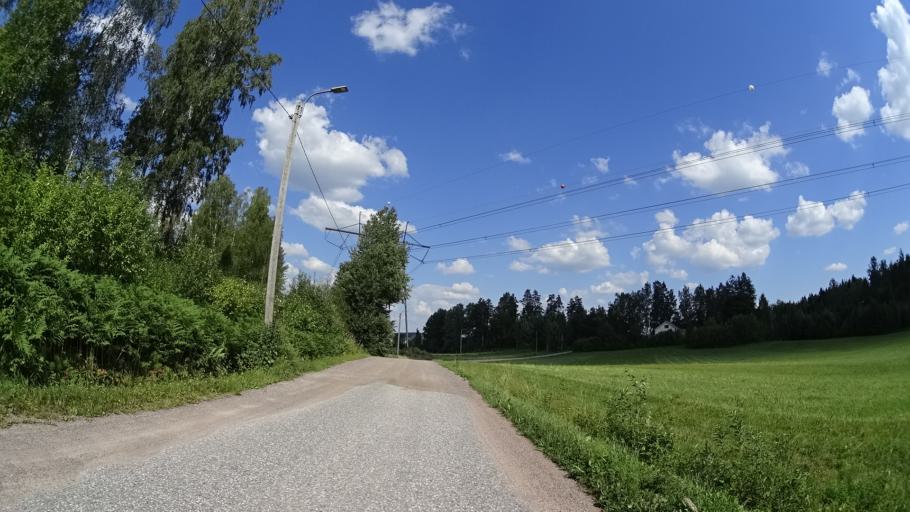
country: FI
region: Uusimaa
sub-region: Helsinki
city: Teekkarikylae
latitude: 60.3027
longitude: 24.8800
